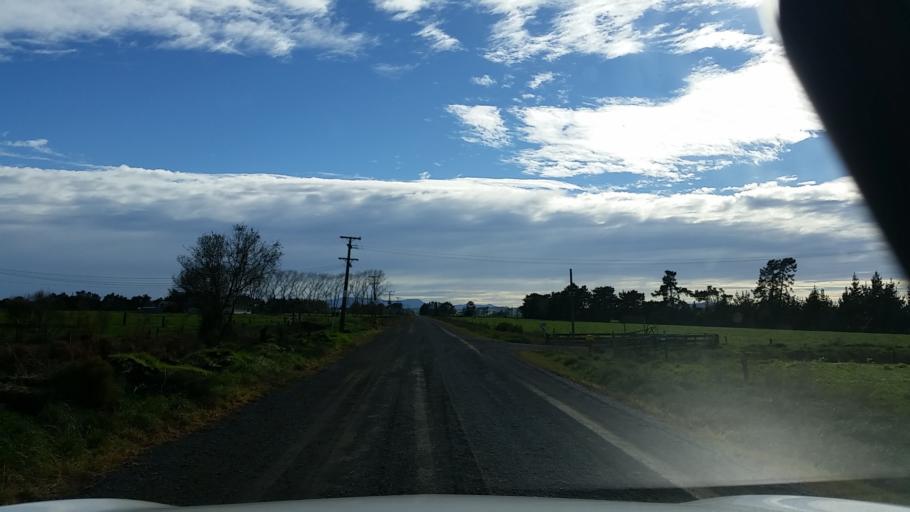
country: NZ
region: Waikato
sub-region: Hamilton City
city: Hamilton
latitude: -37.6710
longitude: 175.4404
